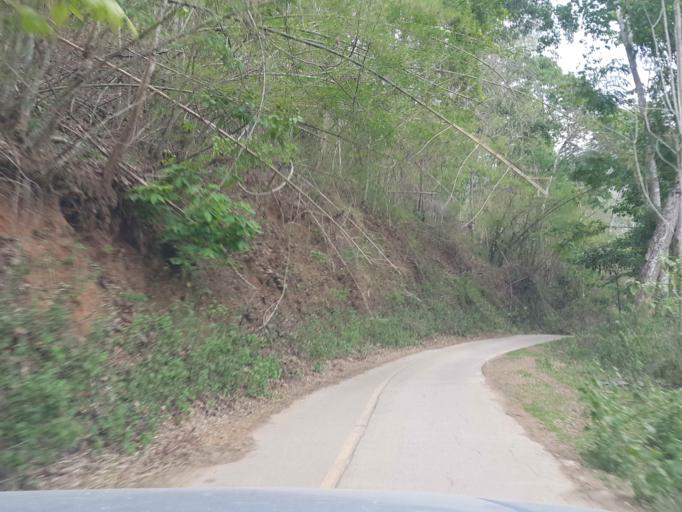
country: TH
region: Chiang Mai
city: Wiang Haeng
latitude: 19.3783
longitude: 98.7498
